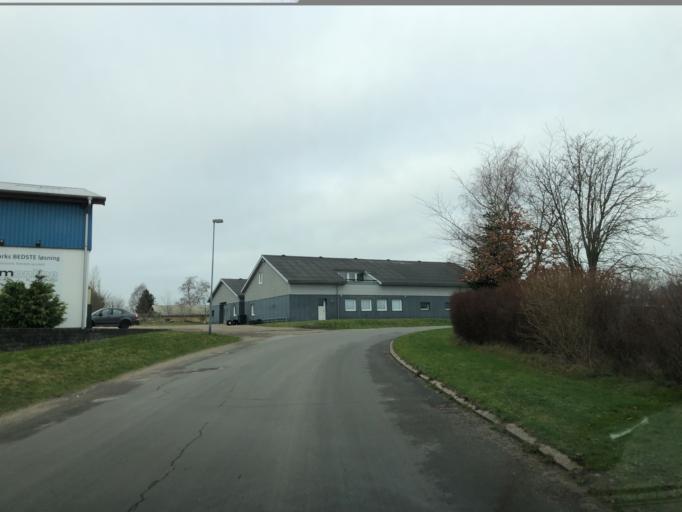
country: DK
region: Central Jutland
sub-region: Viborg Kommune
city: Stoholm
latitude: 56.4865
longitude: 9.1562
